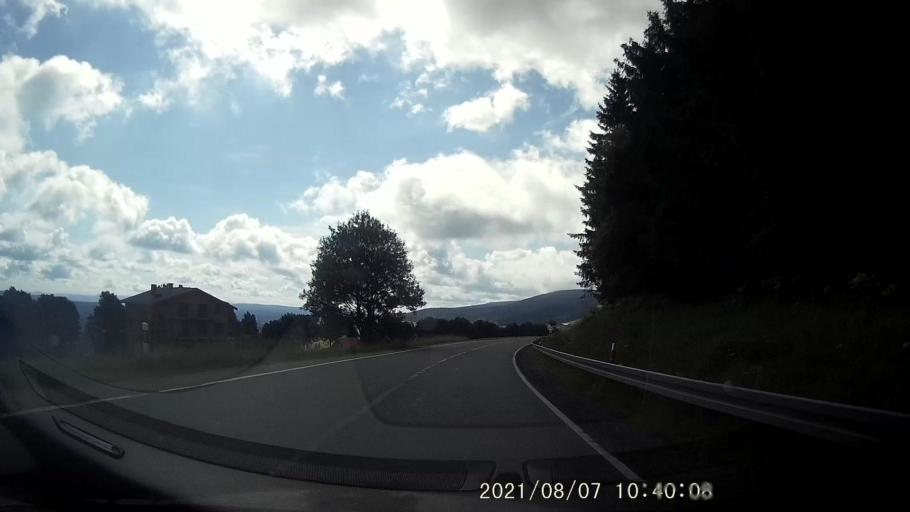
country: PL
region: Lower Silesian Voivodeship
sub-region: Powiat klodzki
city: Duszniki-Zdroj
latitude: 50.3464
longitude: 16.3827
